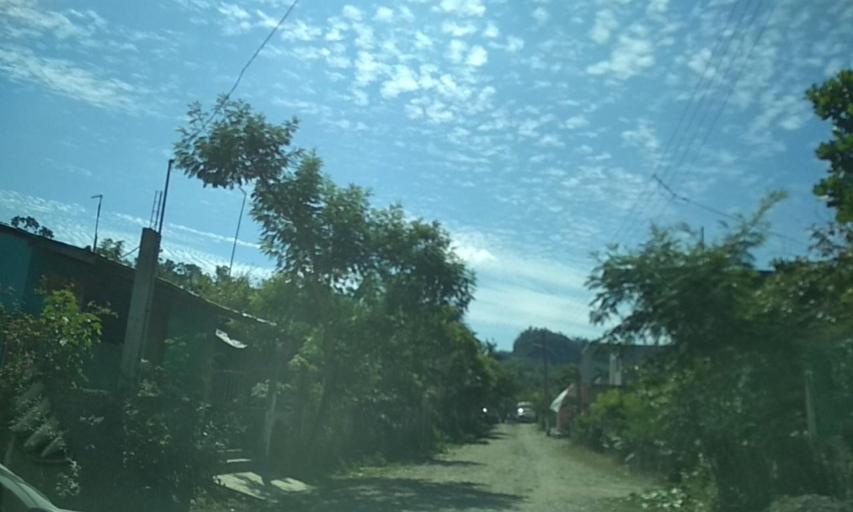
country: MX
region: Veracruz
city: Cazones de Herrera
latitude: 20.6425
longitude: -97.3065
